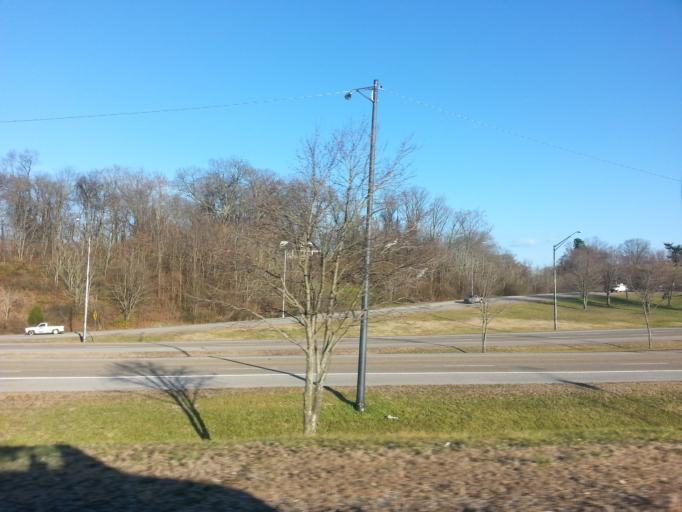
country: US
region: Tennessee
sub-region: Knox County
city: Knoxville
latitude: 35.9588
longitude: -83.8980
